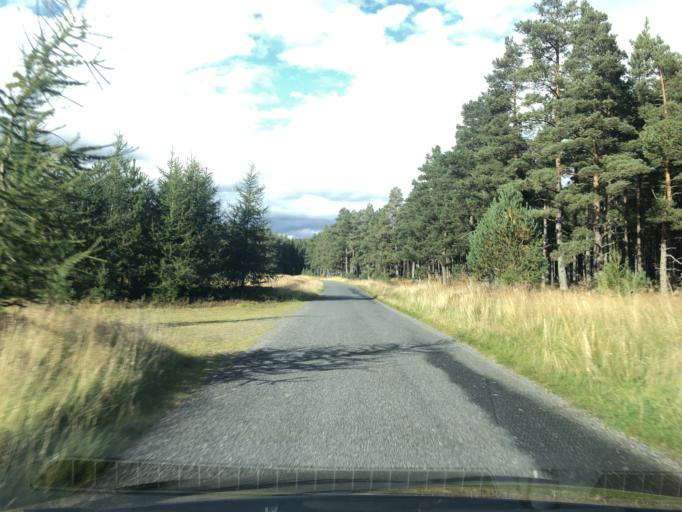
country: GB
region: Scotland
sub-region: Highland
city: Aviemore
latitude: 57.0953
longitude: -3.8922
